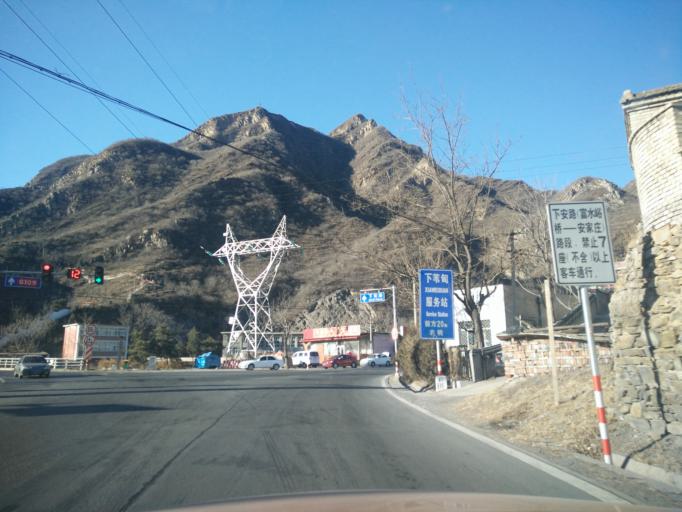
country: CN
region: Beijing
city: Miaofengshan
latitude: 40.0001
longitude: 116.0188
